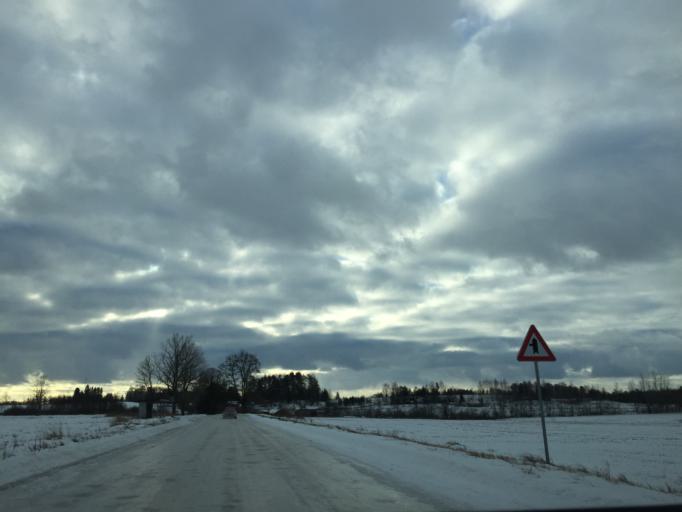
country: LV
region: Lielvarde
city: Lielvarde
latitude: 56.5850
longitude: 24.7343
